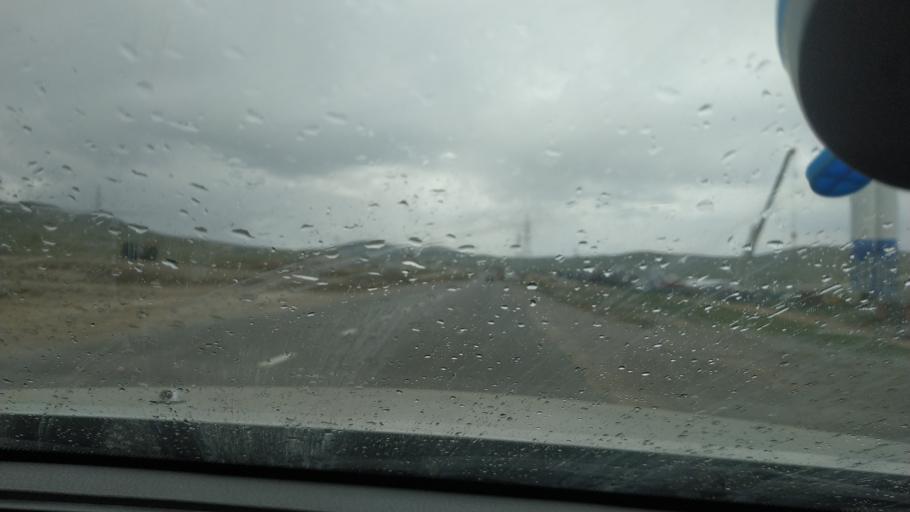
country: MN
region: Ulaanbaatar
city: Ulaanbaatar
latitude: 47.8213
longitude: 106.7617
